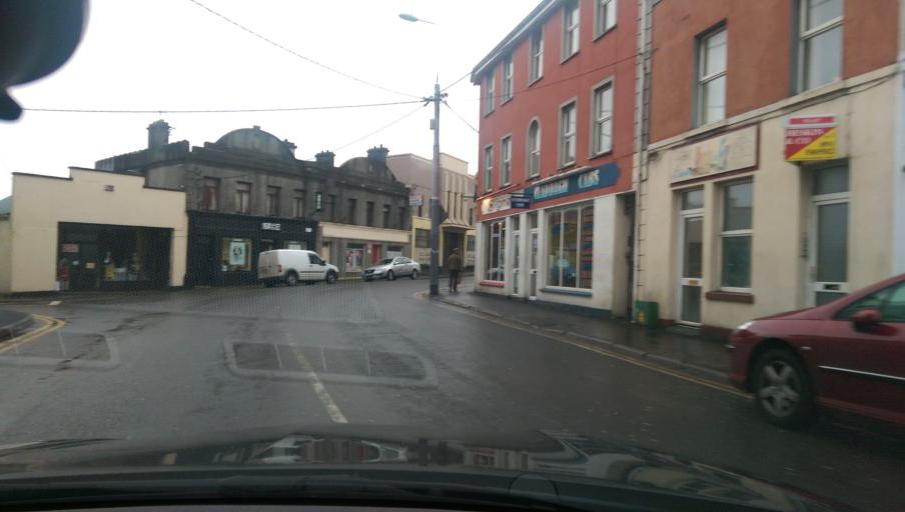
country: IE
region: Connaught
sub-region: County Galway
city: Gaillimh
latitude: 53.2701
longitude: -9.0590
